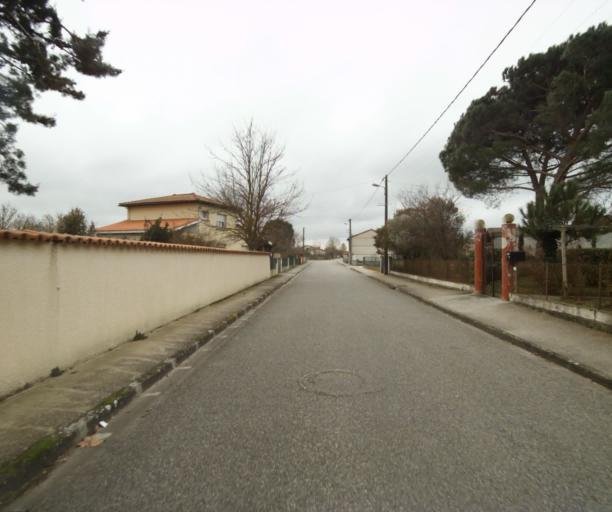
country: FR
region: Midi-Pyrenees
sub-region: Departement de l'Ariege
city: Mazeres
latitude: 43.2482
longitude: 1.6810
